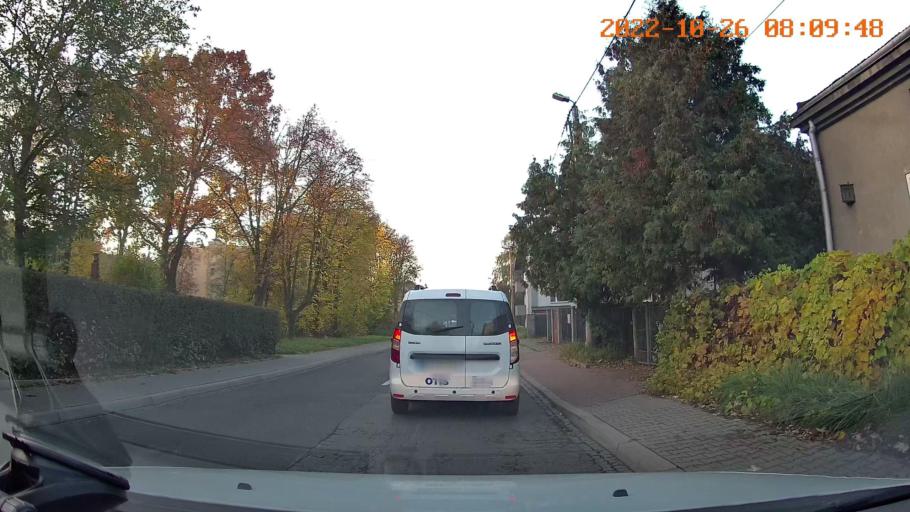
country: PL
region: Lesser Poland Voivodeship
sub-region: Krakow
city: Krakow
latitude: 50.0844
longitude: 19.9161
